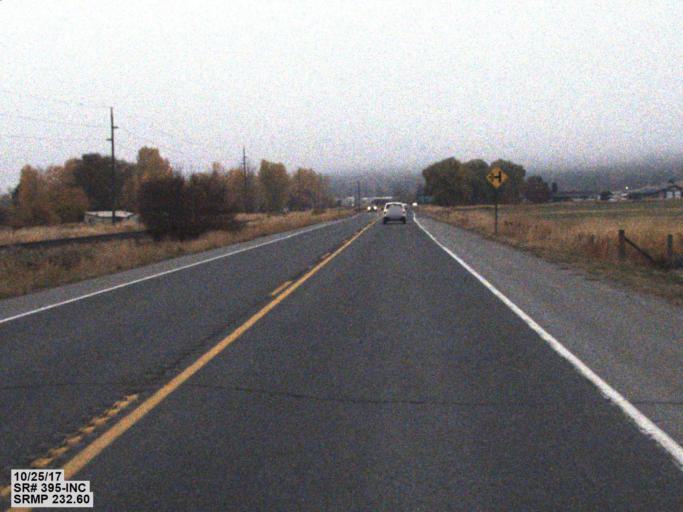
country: US
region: Washington
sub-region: Stevens County
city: Colville
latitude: 48.5757
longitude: -117.9499
